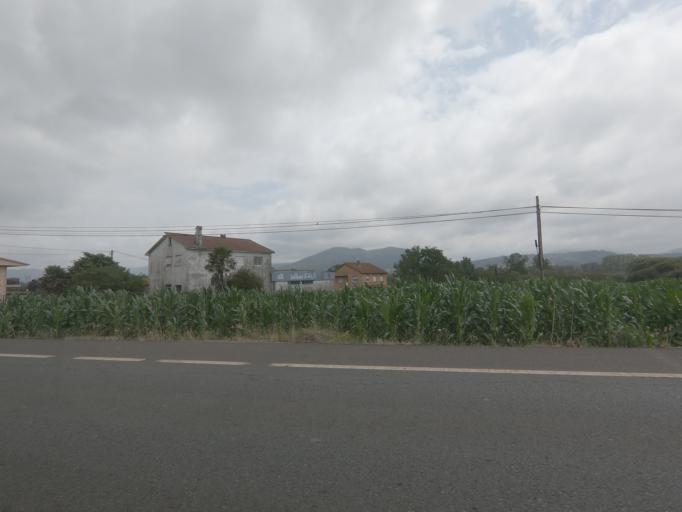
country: ES
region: Galicia
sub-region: Provincia de Pontevedra
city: O Rosal
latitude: 41.9199
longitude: -8.8128
